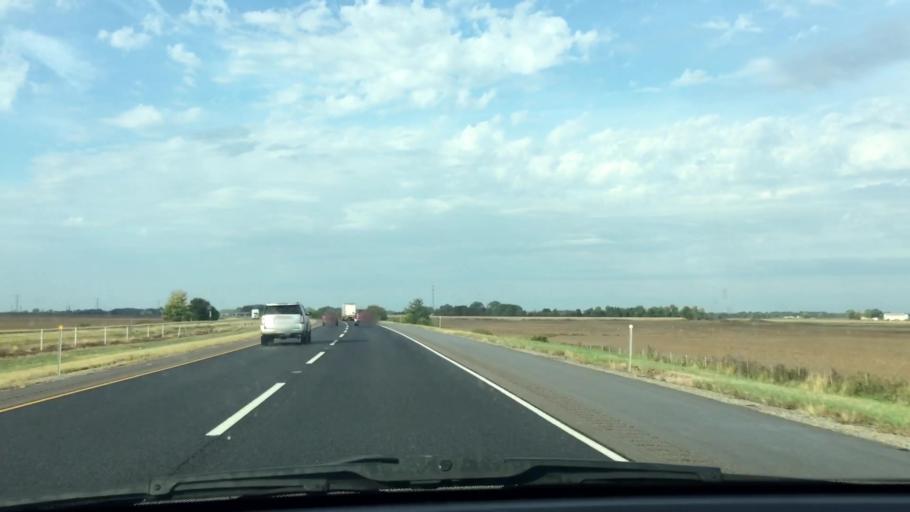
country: US
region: Illinois
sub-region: Lee County
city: Dixon
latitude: 41.7790
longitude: -89.5632
